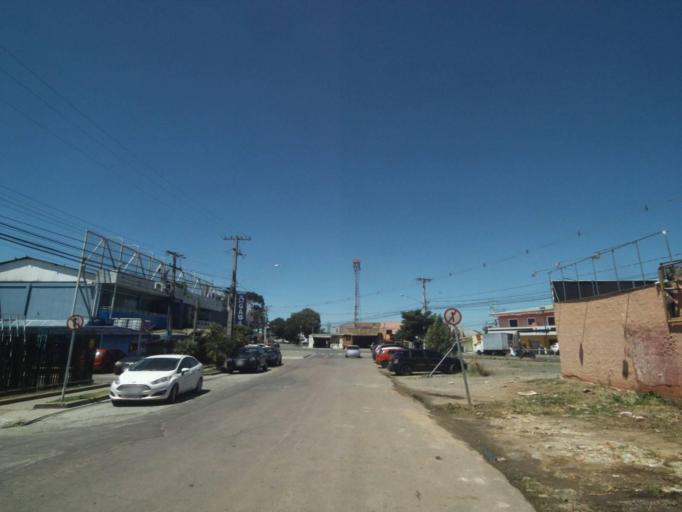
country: BR
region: Parana
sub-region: Curitiba
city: Curitiba
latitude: -25.4818
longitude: -49.3448
